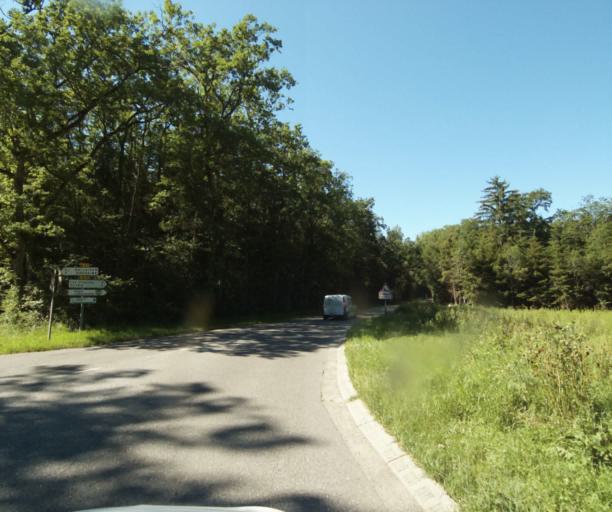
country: FR
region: Rhone-Alpes
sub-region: Departement de la Haute-Savoie
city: Ballaison
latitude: 46.2833
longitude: 6.3468
